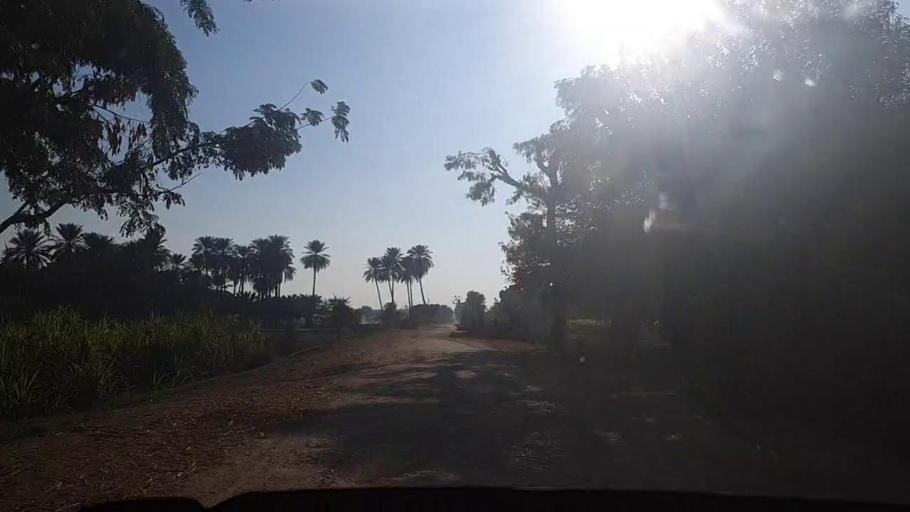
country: PK
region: Sindh
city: Gambat
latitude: 27.3551
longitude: 68.4541
